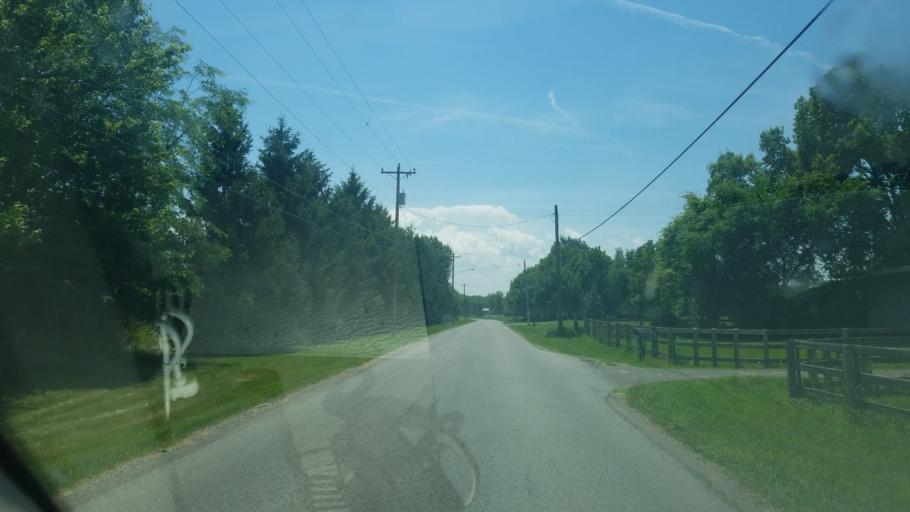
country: US
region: Ohio
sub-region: Hancock County
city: Findlay
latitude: 41.0116
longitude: -83.6360
